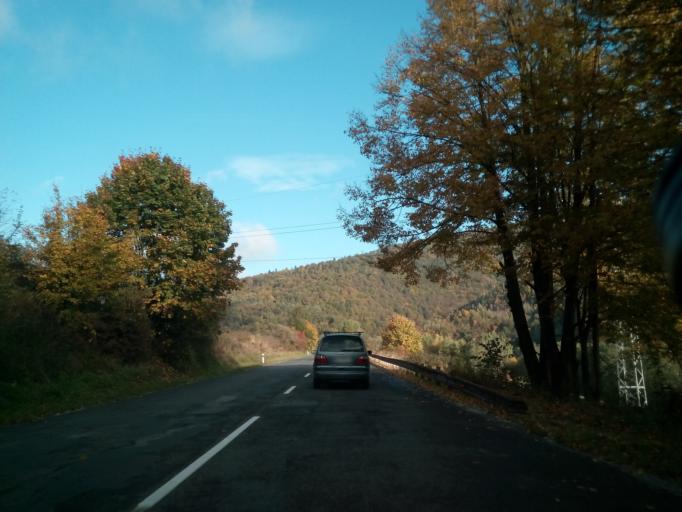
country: SK
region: Kosicky
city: Gelnica
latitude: 48.8998
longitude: 20.9871
